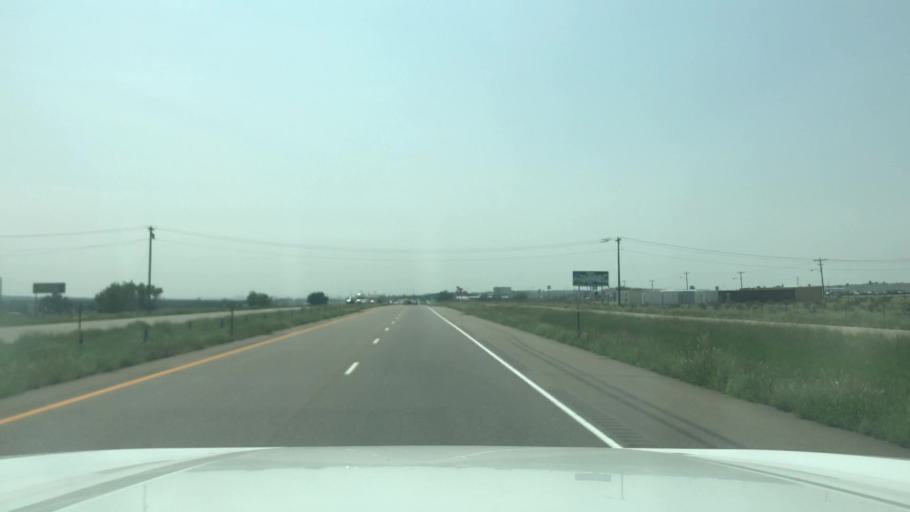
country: US
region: Colorado
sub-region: Pueblo County
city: Pueblo West
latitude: 38.3562
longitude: -104.6206
